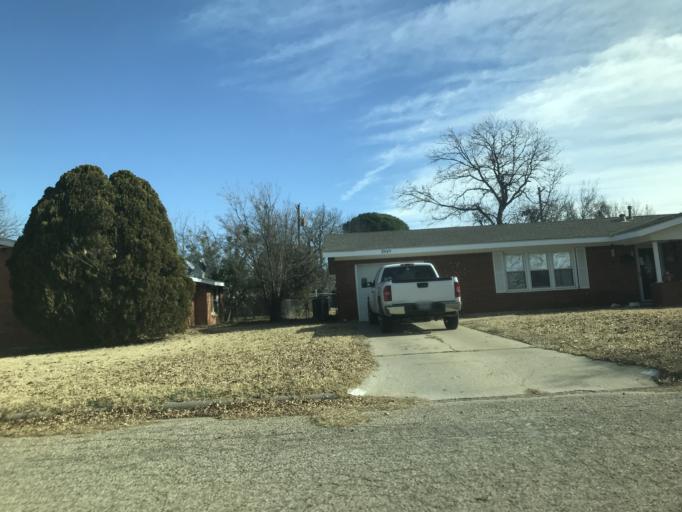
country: US
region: Texas
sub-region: Taylor County
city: Abilene
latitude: 32.4788
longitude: -99.7150
